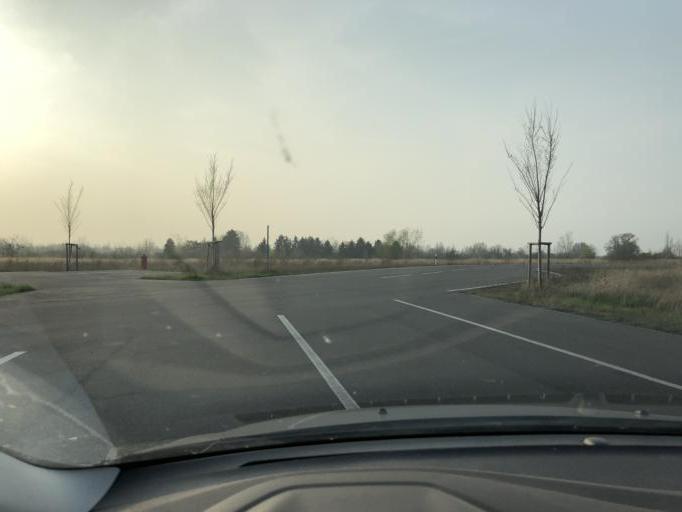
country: DE
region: Saxony
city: Dobernitz
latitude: 51.4950
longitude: 12.3229
